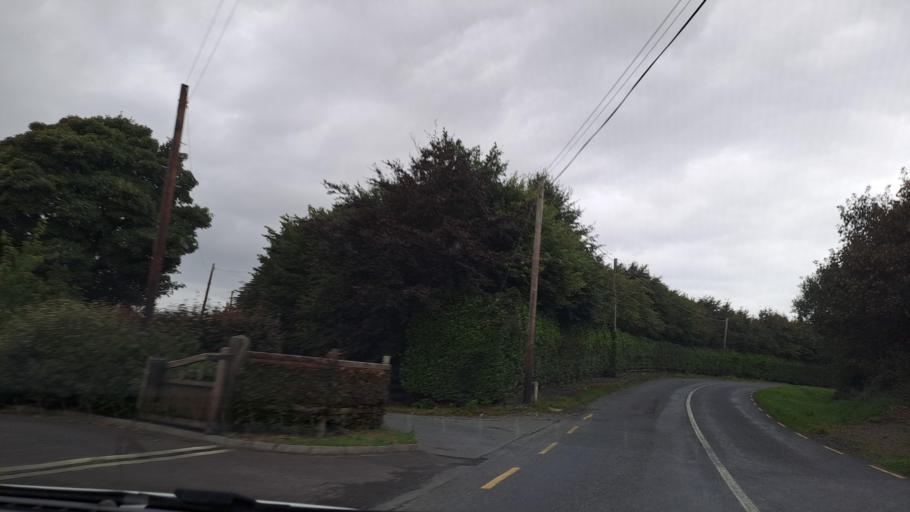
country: IE
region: Ulster
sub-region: An Cabhan
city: Bailieborough
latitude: 54.0049
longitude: -6.9094
